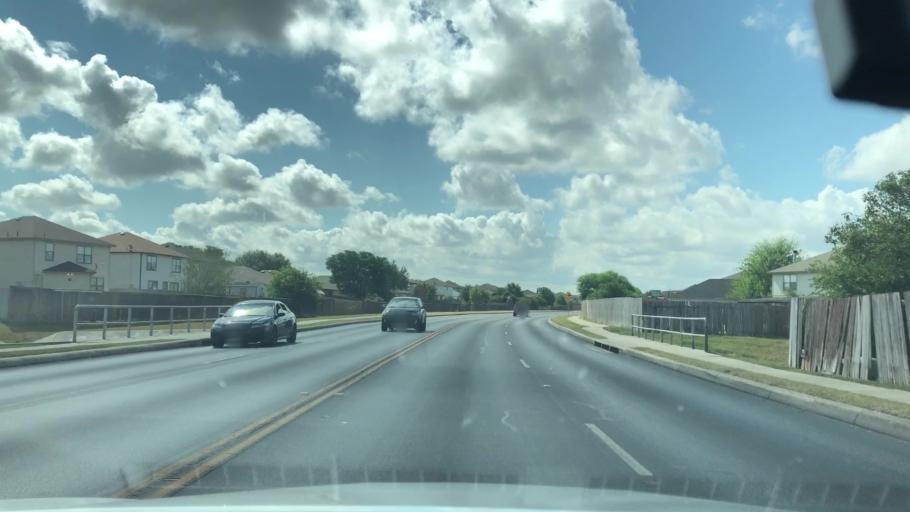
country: US
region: Texas
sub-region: Bexar County
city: Converse
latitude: 29.4947
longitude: -98.3167
